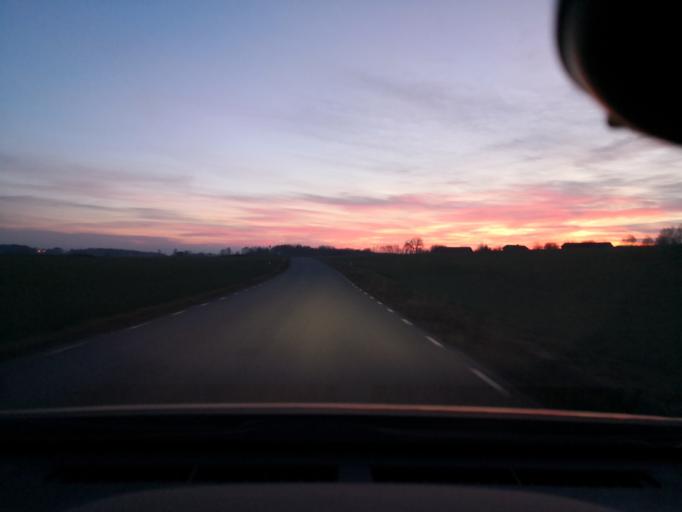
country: SE
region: OErebro
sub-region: Lindesbergs Kommun
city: Frovi
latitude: 59.3436
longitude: 15.3906
